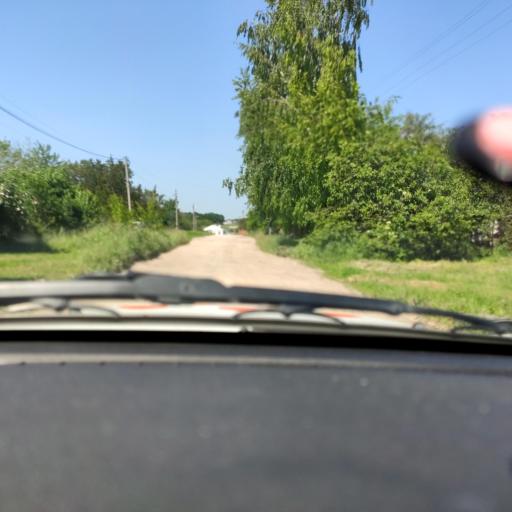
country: RU
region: Voronezj
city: Devitsa
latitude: 51.5960
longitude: 38.9887
